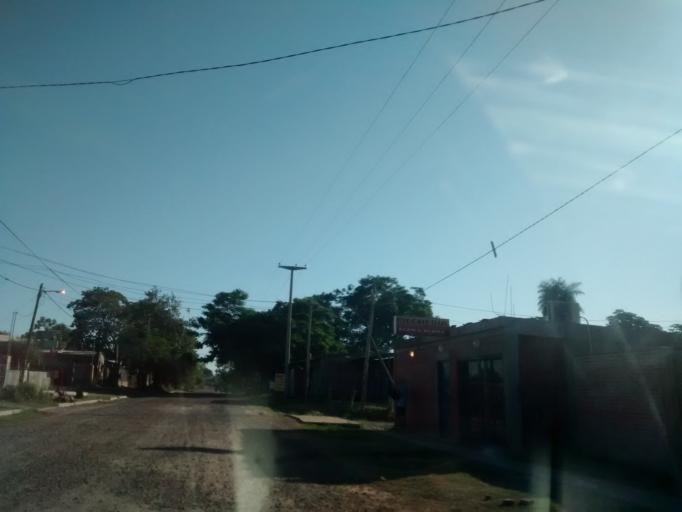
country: AR
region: Chaco
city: Resistencia
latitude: -27.4619
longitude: -58.9625
